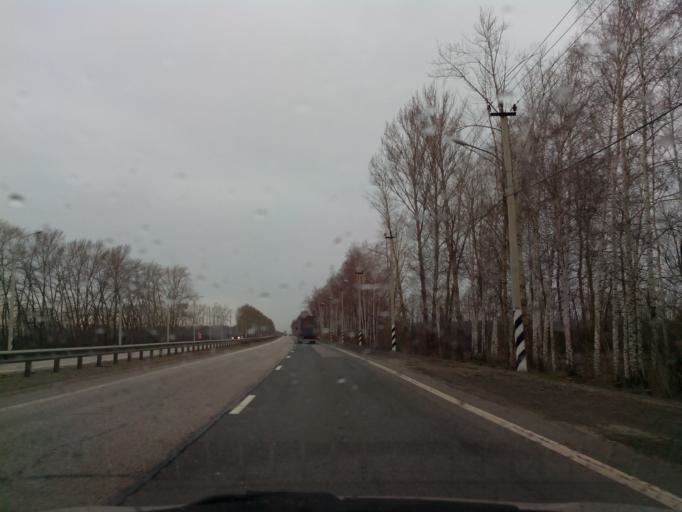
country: RU
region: Tambov
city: Selezni
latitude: 52.7533
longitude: 41.1732
